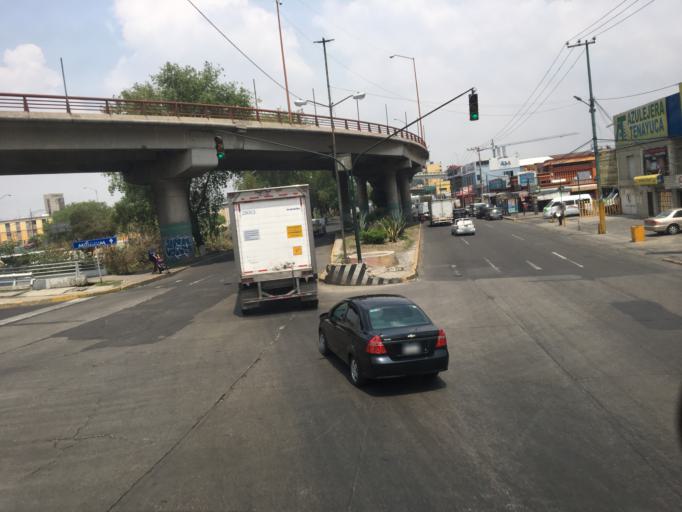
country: MX
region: Mexico
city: Tlalnepantla
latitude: 19.5302
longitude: -99.1698
